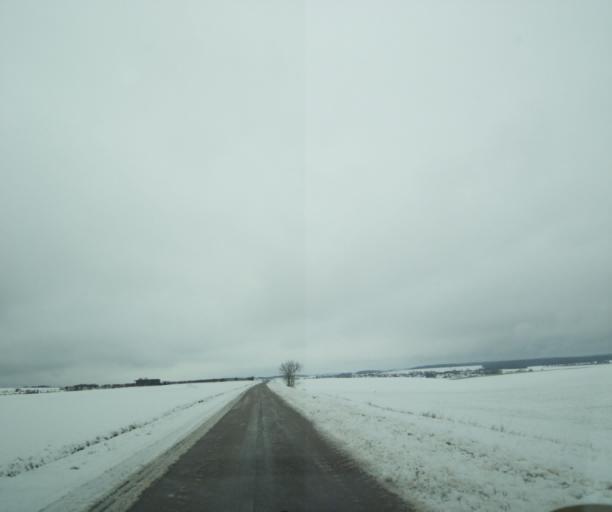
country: FR
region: Champagne-Ardenne
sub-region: Departement de la Haute-Marne
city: Laneuville-a-Remy
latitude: 48.3993
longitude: 4.8598
